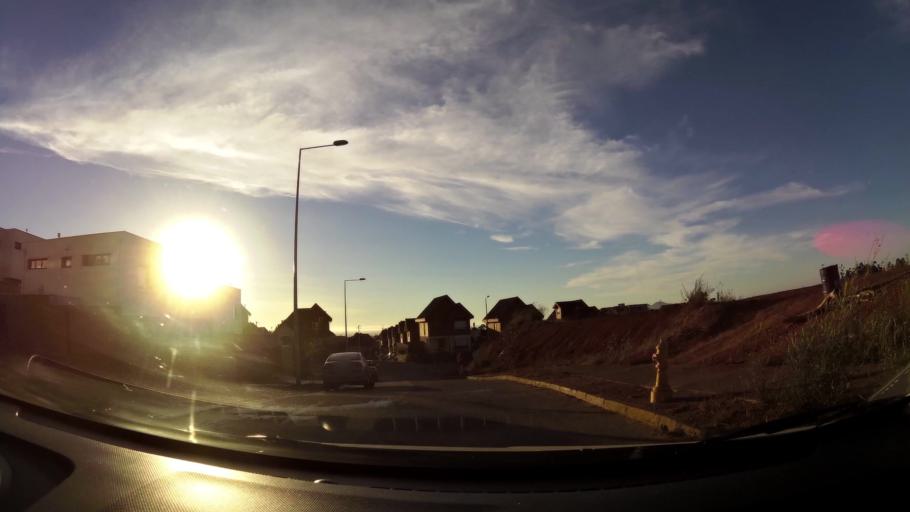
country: CL
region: Biobio
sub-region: Provincia de Concepcion
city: Concepcion
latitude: -36.8548
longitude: -73.0907
